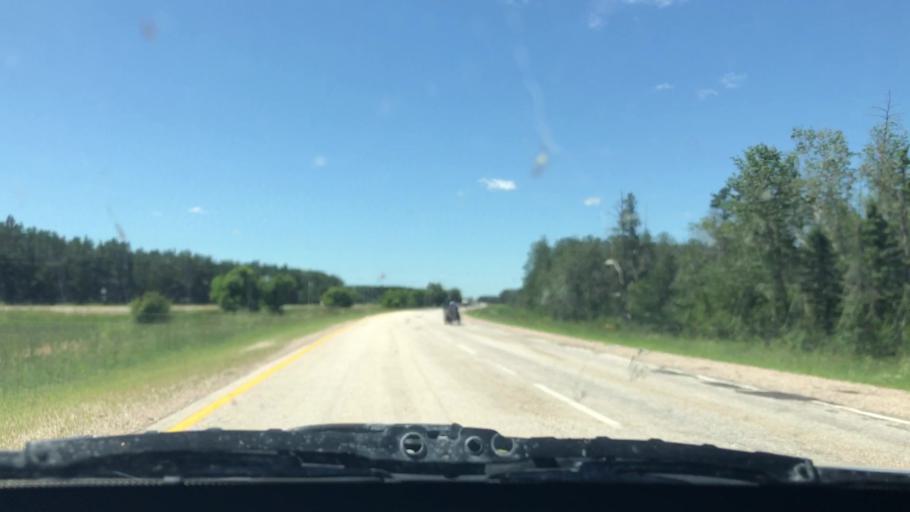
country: CA
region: Manitoba
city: La Broquerie
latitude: 49.6563
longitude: -96.1501
